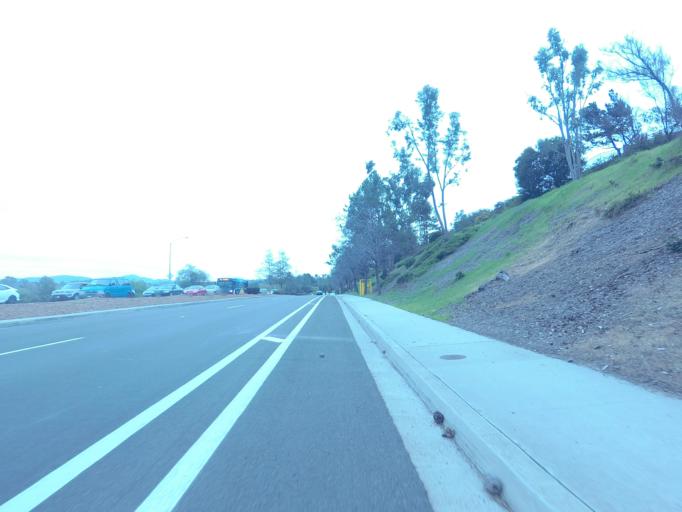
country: US
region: California
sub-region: San Diego County
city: Vista
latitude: 33.2447
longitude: -117.2805
